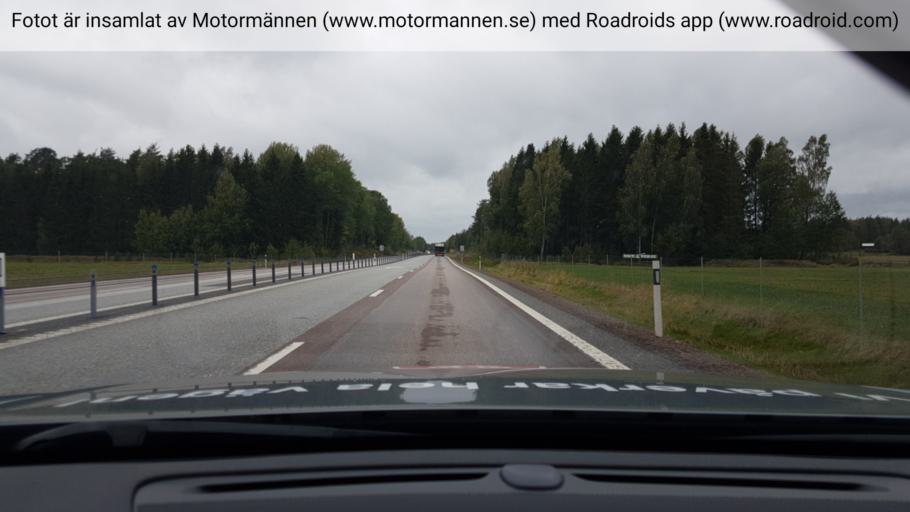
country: SE
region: Vaermland
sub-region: Kristinehamns Kommun
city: Kristinehamn
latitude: 59.3790
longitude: 13.9107
